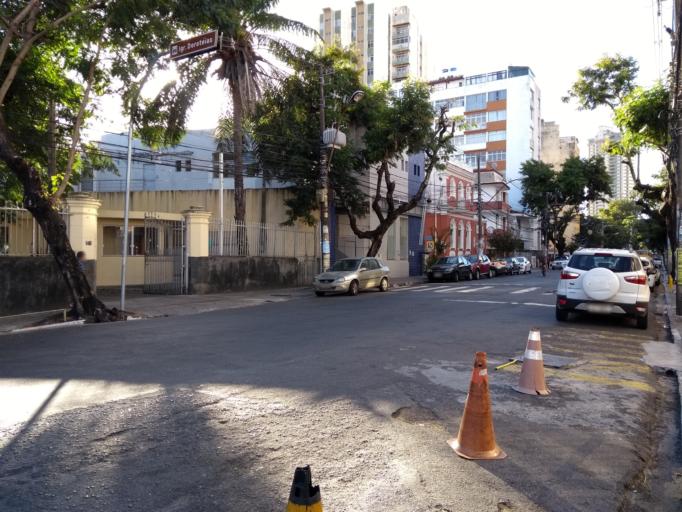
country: BR
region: Bahia
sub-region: Salvador
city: Salvador
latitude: -12.9904
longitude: -38.5186
